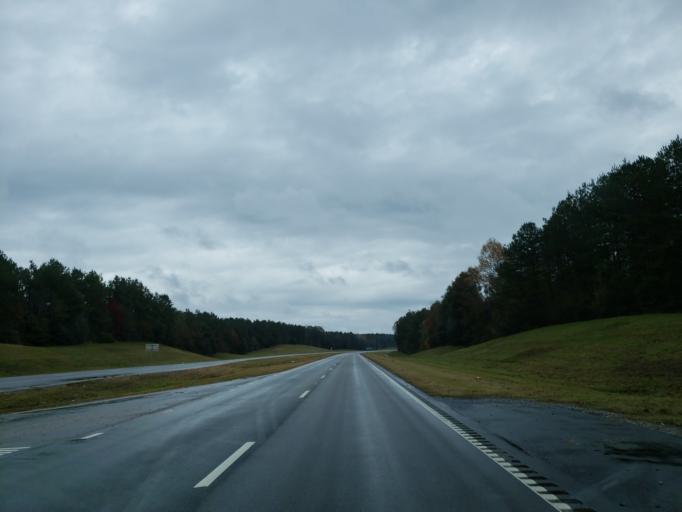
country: US
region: Mississippi
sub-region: Wayne County
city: Waynesboro
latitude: 31.6979
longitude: -88.6582
